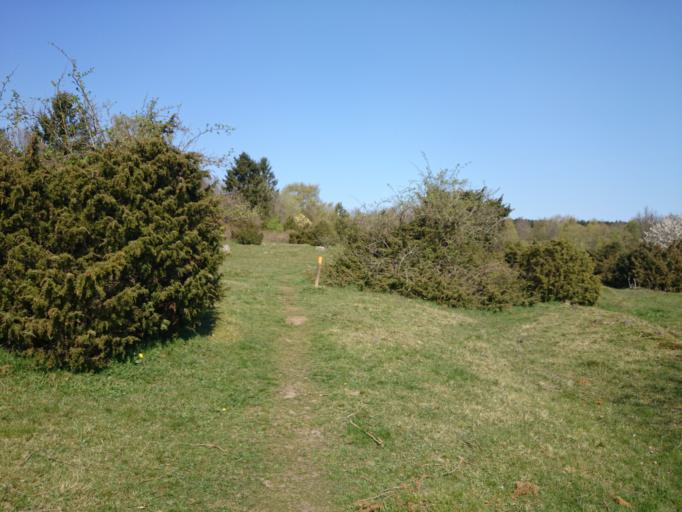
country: SE
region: Skane
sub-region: Lunds Kommun
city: Genarp
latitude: 55.6757
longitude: 13.3833
